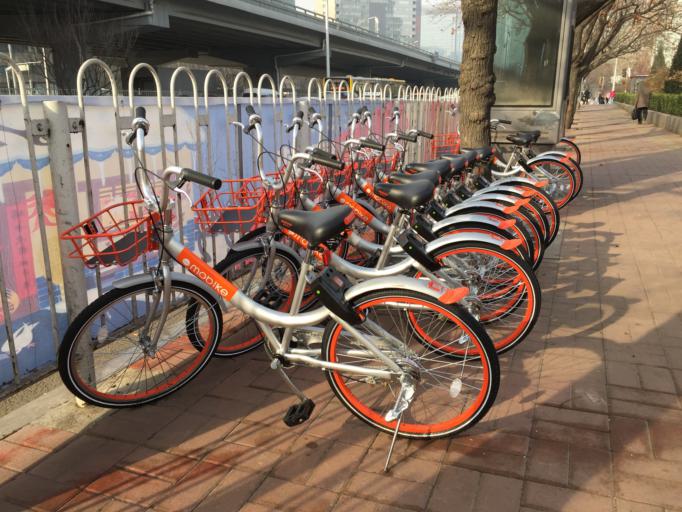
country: CN
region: Beijing
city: Chaowai
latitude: 39.9473
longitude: 116.4559
